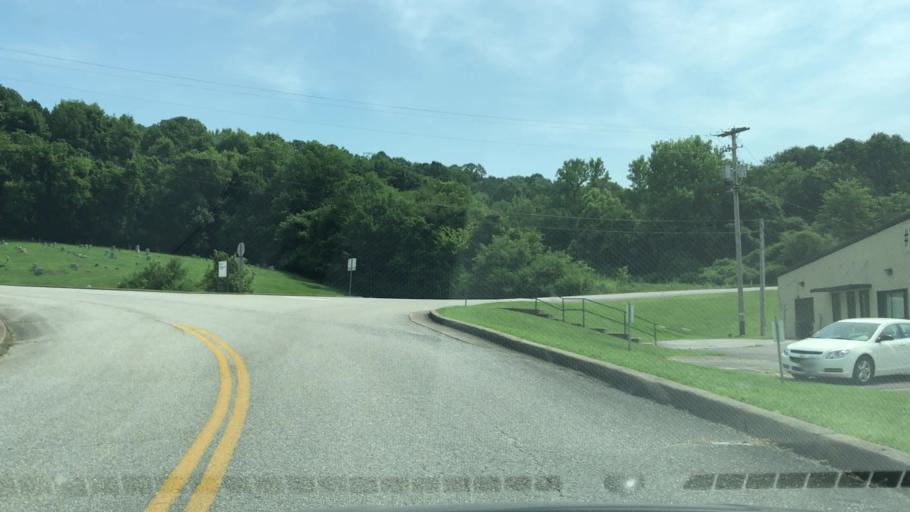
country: US
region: Tennessee
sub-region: Smith County
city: Carthage
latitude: 36.2632
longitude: -85.9493
